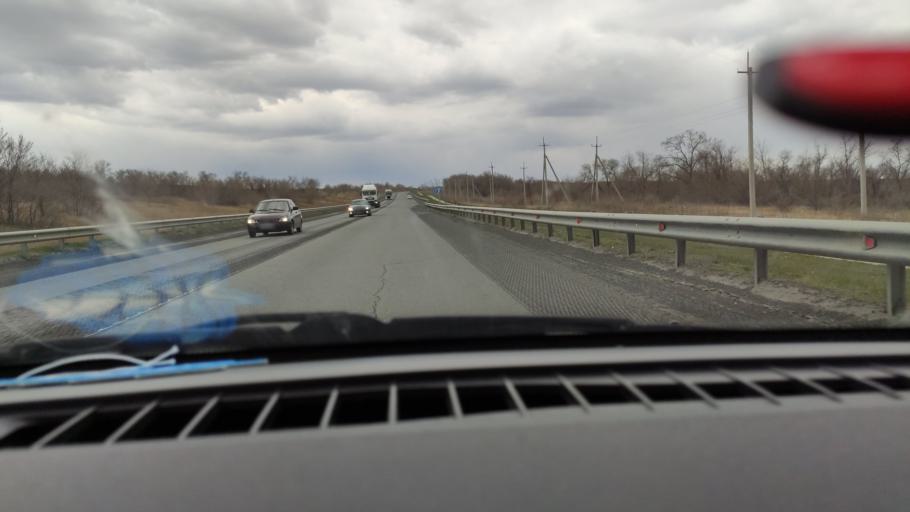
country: RU
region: Saratov
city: Shumeyka
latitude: 51.7797
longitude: 46.1220
